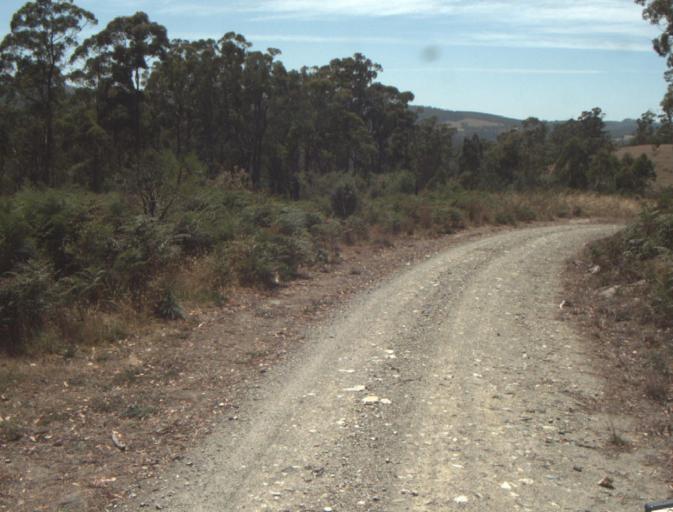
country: AU
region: Tasmania
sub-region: Launceston
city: Mayfield
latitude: -41.2479
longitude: 147.1663
